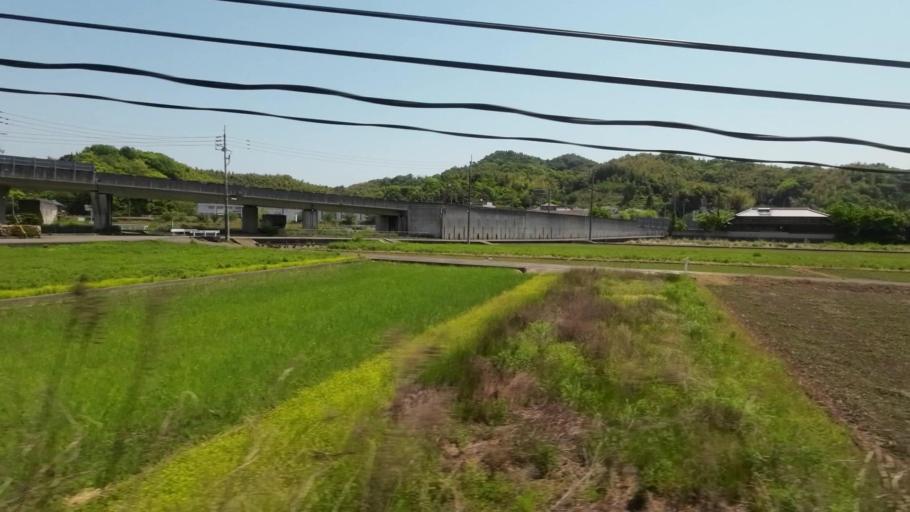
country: JP
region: Ehime
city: Saijo
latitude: 34.0010
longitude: 133.0377
